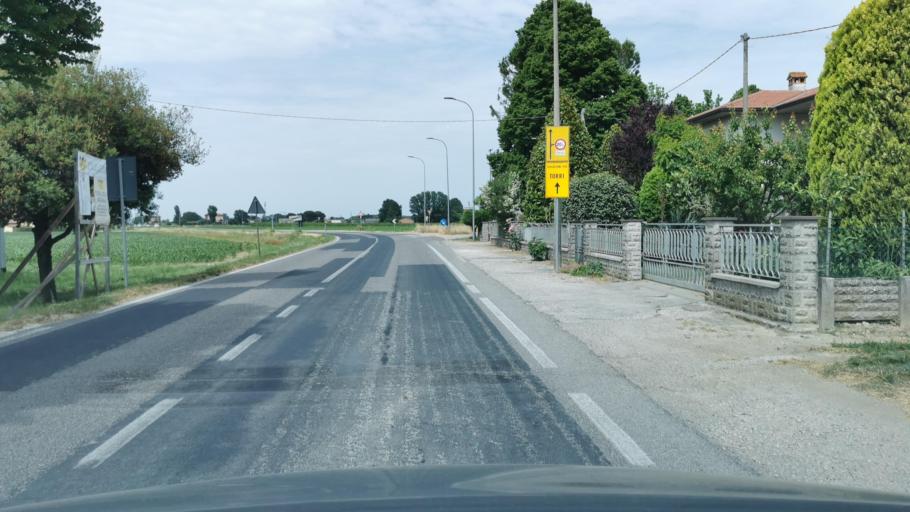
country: IT
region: Emilia-Romagna
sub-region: Provincia di Ravenna
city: Savarna-Conventella
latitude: 44.5038
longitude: 12.1005
